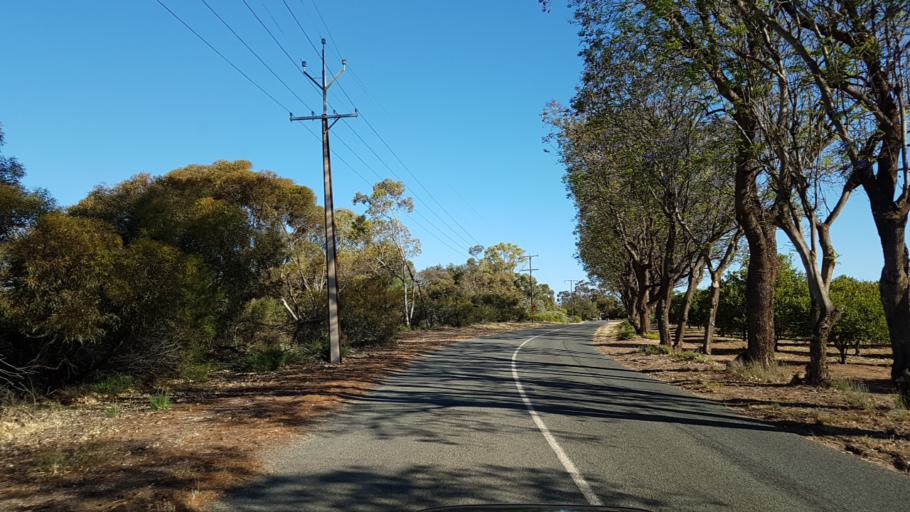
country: AU
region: South Australia
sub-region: Loxton Waikerie
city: Waikerie
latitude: -34.1668
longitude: 140.0360
